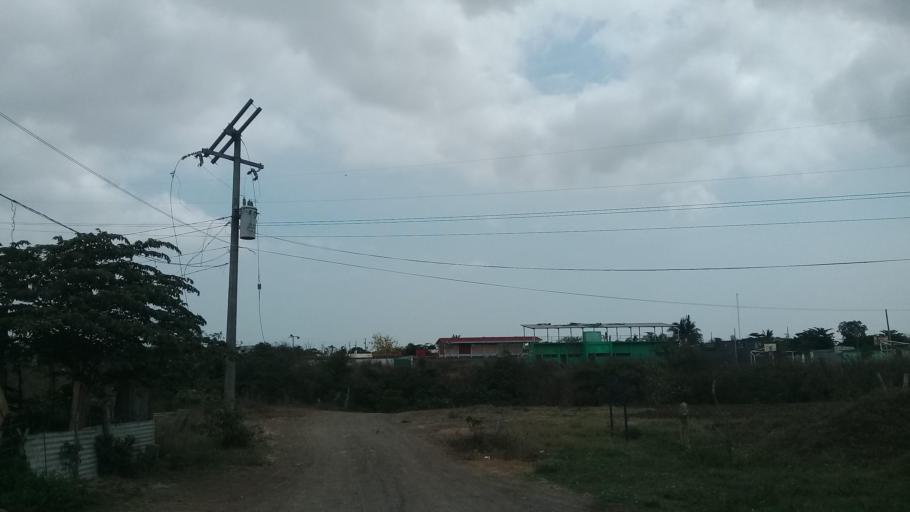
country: MX
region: Veracruz
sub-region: Veracruz
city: Las Amapolas
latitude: 19.1350
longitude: -96.2361
